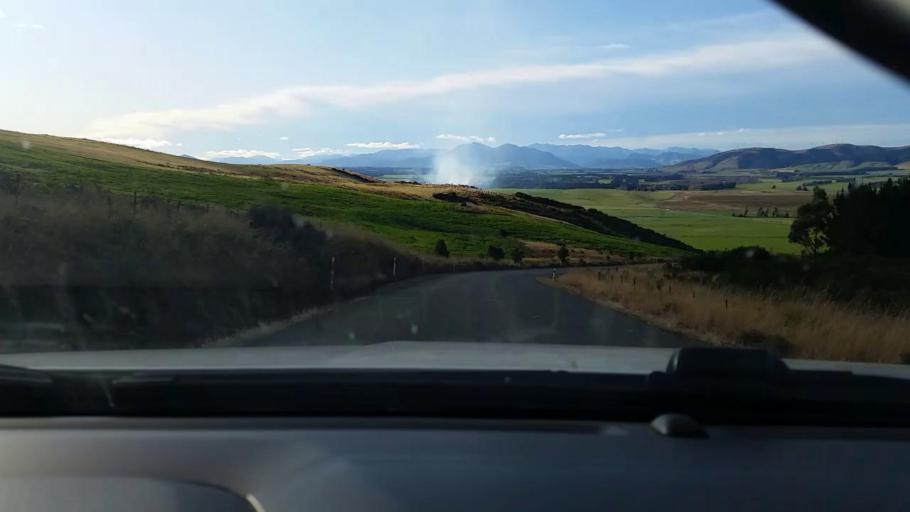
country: NZ
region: Southland
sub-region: Southland District
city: Winton
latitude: -45.8201
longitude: 168.1739
